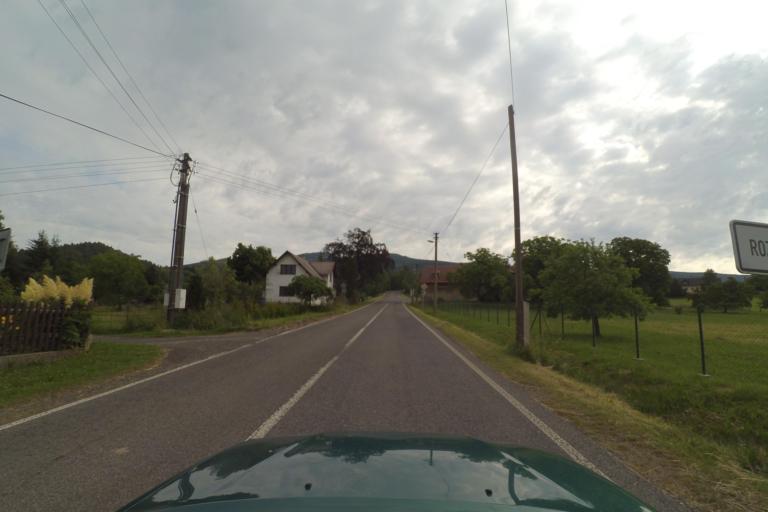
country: CZ
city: Osecna
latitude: 50.7091
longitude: 14.9671
